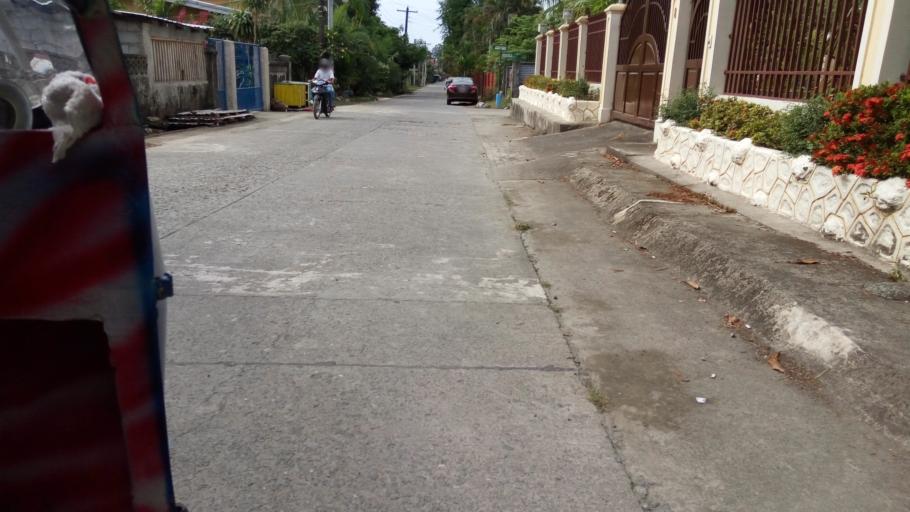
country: PH
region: Ilocos
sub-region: Province of La Union
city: Aringay
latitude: 16.3928
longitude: 120.3551
